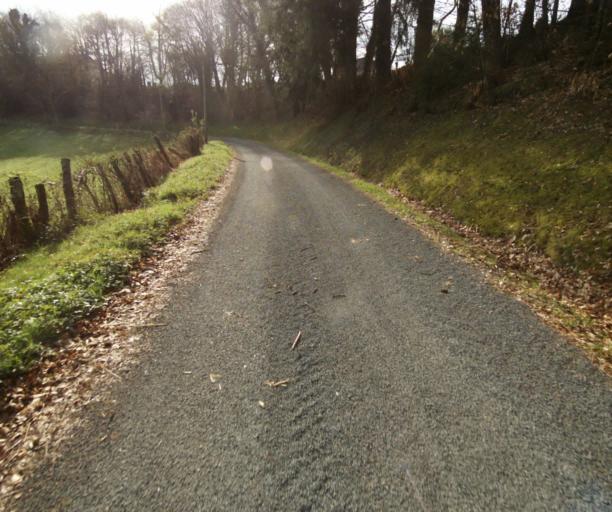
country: FR
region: Limousin
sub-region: Departement de la Correze
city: Naves
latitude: 45.3257
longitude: 1.8215
